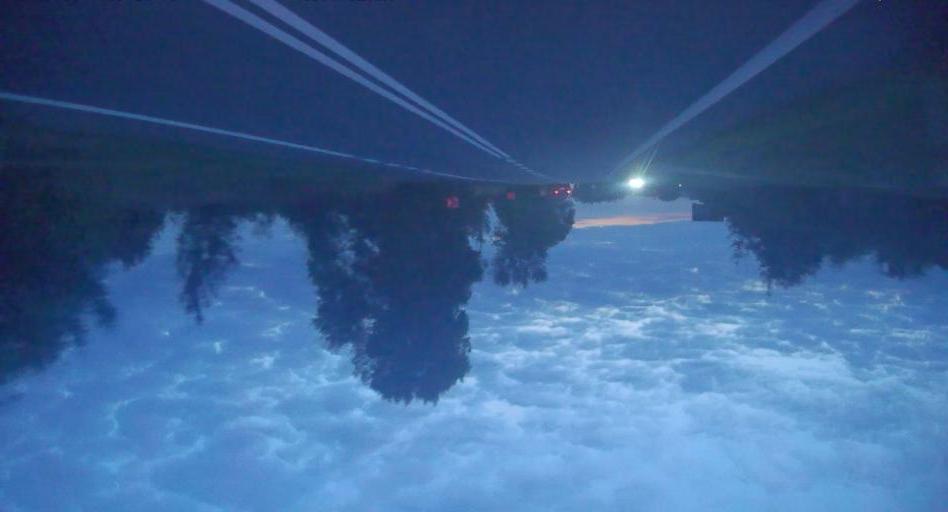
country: PL
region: Silesian Voivodeship
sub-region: Powiat klobucki
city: Kamyk
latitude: 50.8806
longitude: 18.9940
